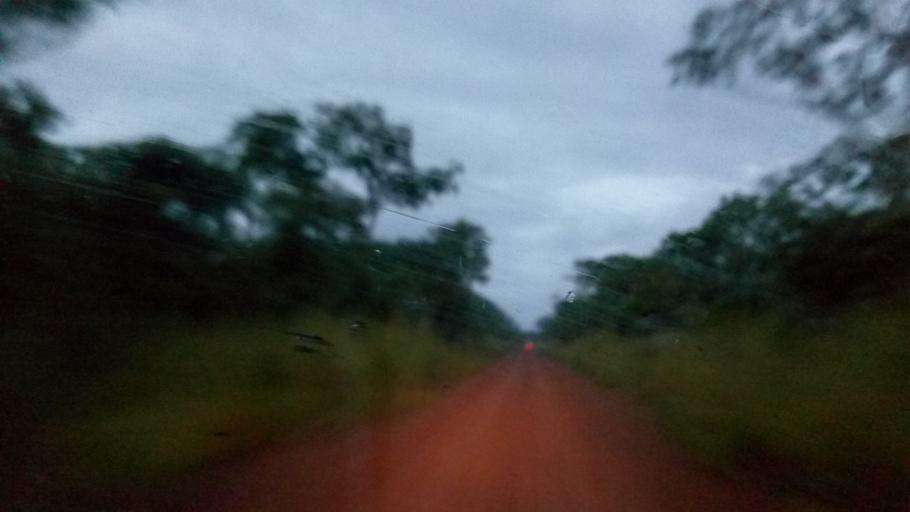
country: ZM
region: Luapula
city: Nchelenge
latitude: -9.8084
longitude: 28.1426
